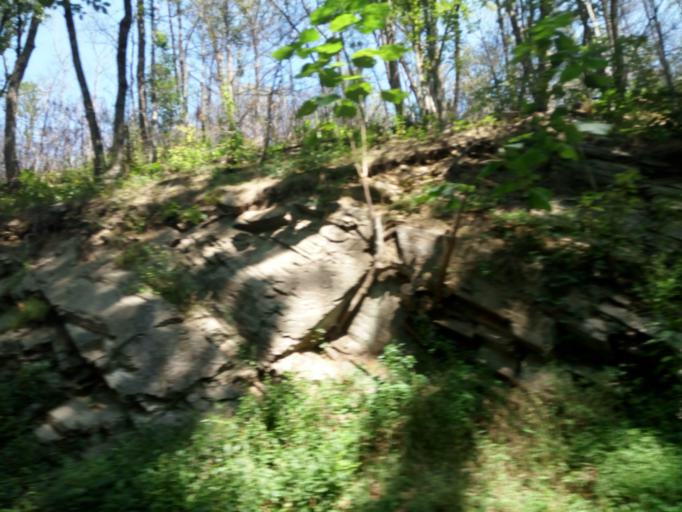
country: US
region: Tennessee
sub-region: Sevier County
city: Gatlinburg
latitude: 35.7317
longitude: -83.5235
